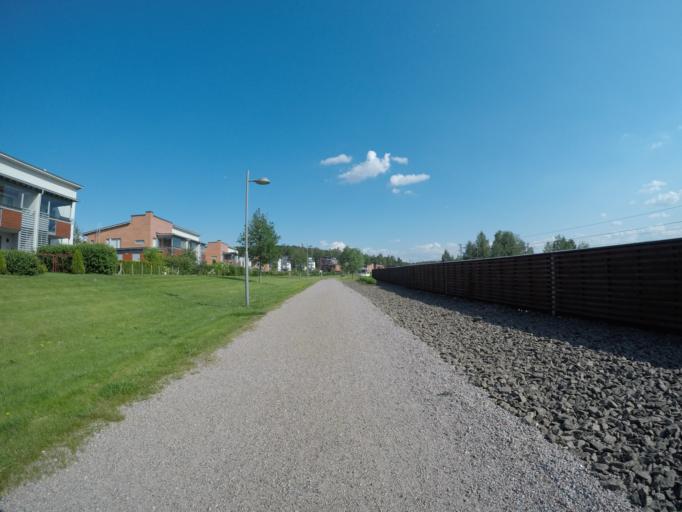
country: FI
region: Haeme
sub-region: Haemeenlinna
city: Haemeenlinna
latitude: 61.0122
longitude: 24.4599
